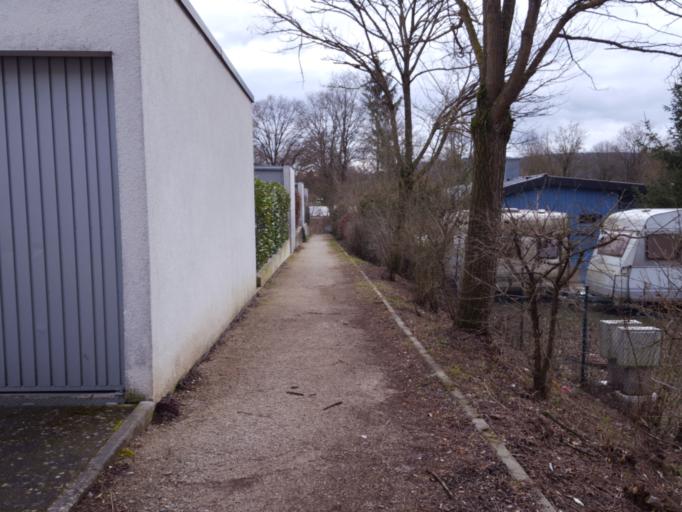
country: DE
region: Baden-Wuerttemberg
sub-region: Tuebingen Region
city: Tuebingen
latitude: 48.5111
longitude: 9.0357
